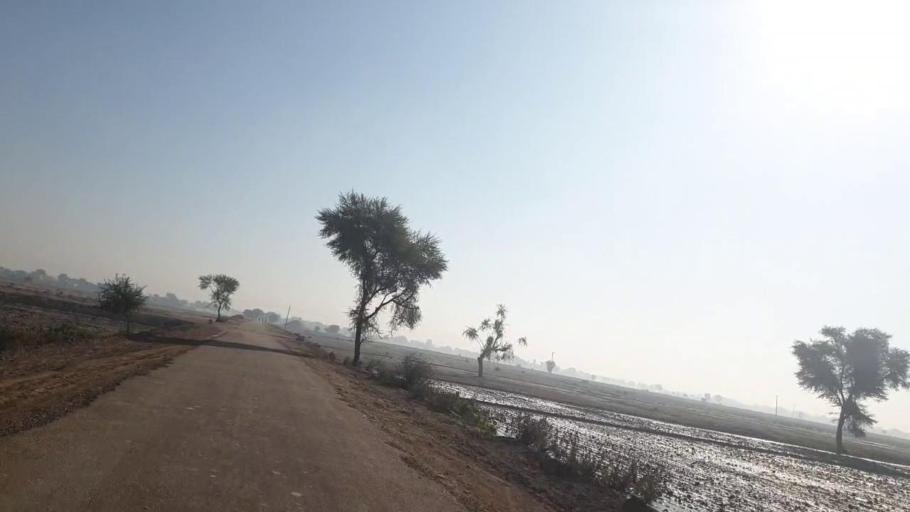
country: PK
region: Sindh
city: Dadu
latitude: 26.6710
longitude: 67.8421
